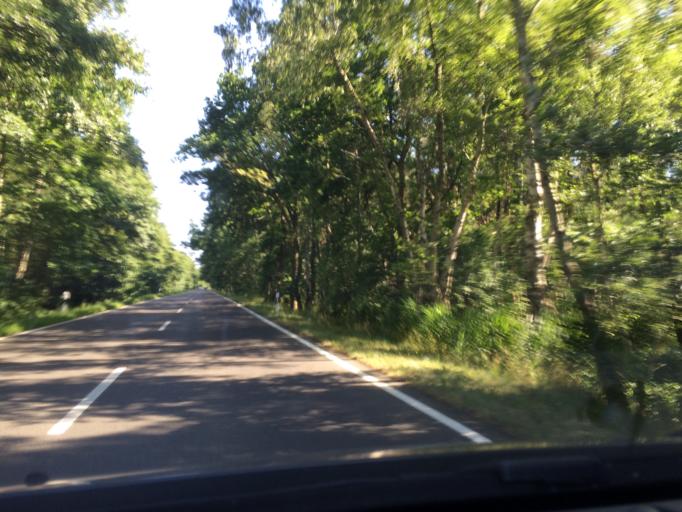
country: DE
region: Mecklenburg-Vorpommern
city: Zingst
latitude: 54.4394
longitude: 12.6483
